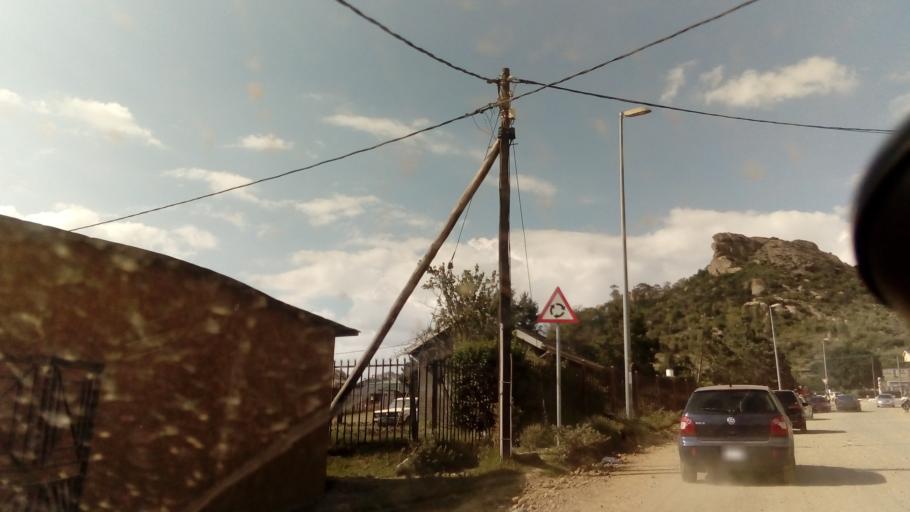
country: LS
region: Maseru
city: Maseru
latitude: -29.3697
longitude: 27.5356
